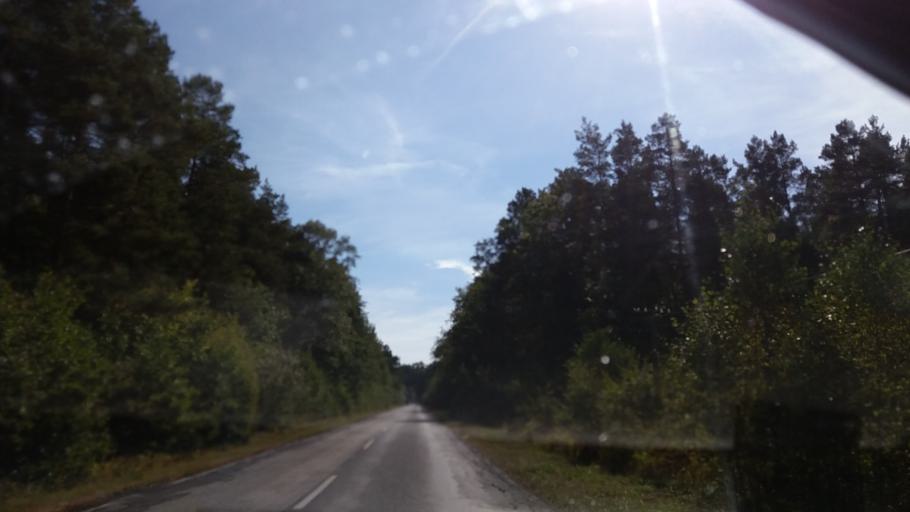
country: PL
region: Lubusz
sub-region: Powiat strzelecko-drezdenecki
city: Drezdenko
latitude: 52.7973
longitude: 15.8338
